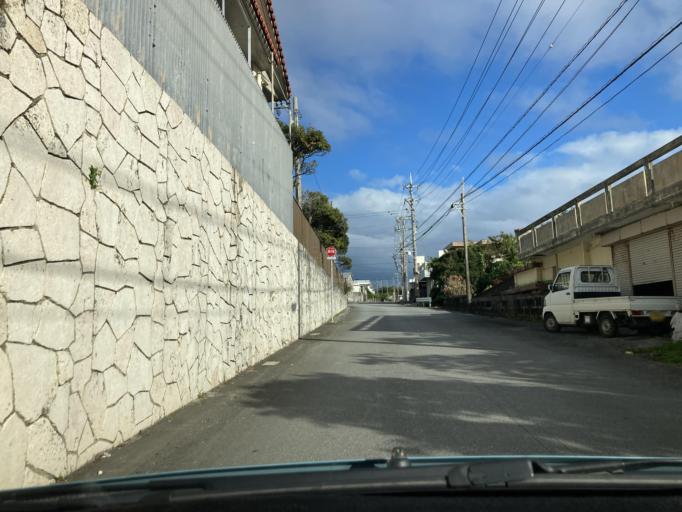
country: JP
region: Okinawa
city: Itoman
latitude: 26.1160
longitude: 127.6765
